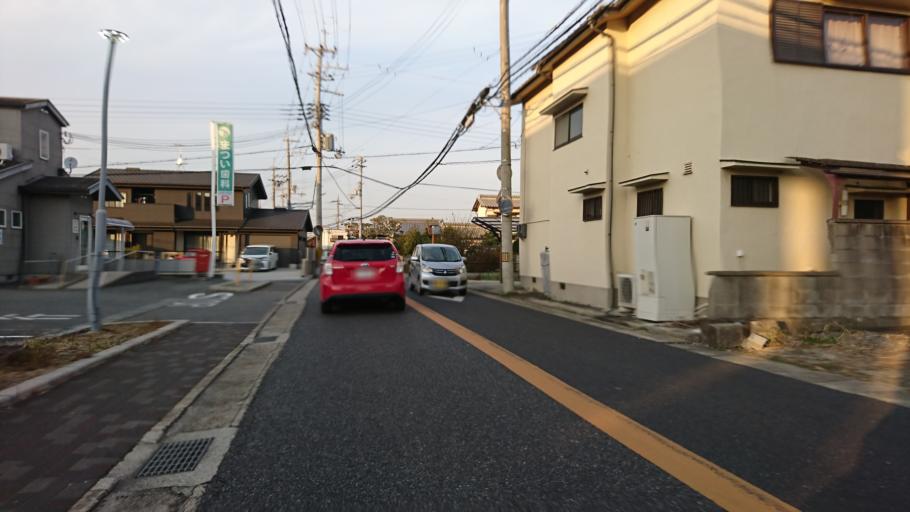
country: JP
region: Hyogo
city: Kakogawacho-honmachi
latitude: 34.7776
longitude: 134.8767
